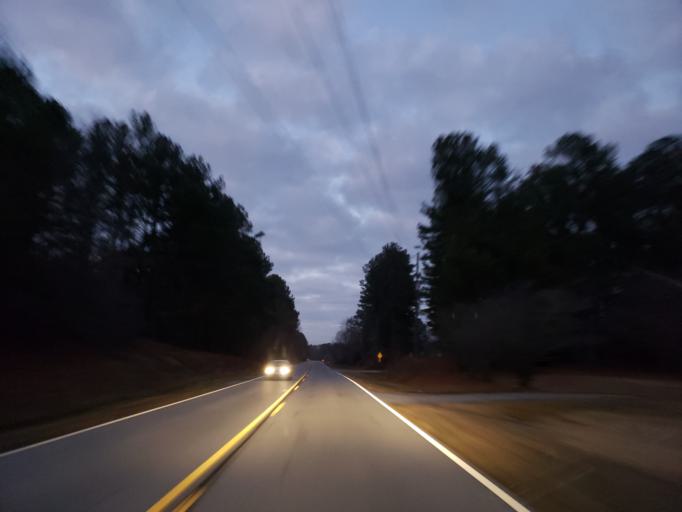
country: US
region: Georgia
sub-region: Carroll County
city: Temple
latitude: 33.8225
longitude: -85.0440
